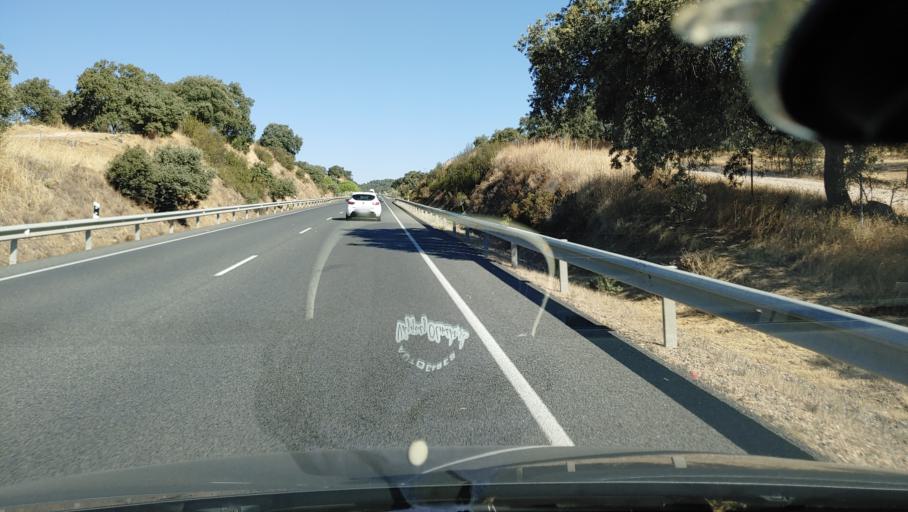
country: ES
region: Andalusia
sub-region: Province of Cordoba
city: Obejo
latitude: 38.0128
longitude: -4.8052
